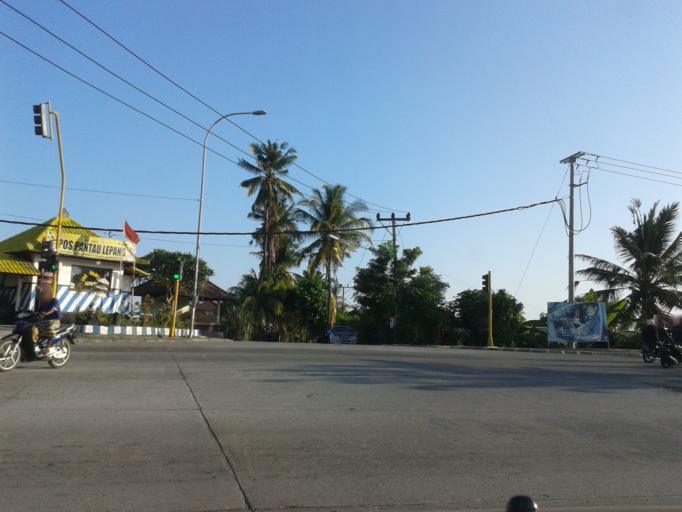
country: ID
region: Bali
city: Semarapura
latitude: -8.5682
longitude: 115.3849
